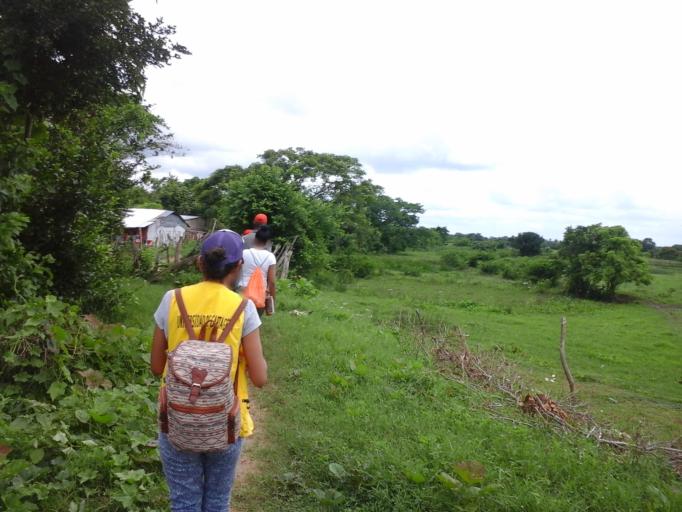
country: CO
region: Bolivar
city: San Pablo
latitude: 10.1453
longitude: -75.2761
